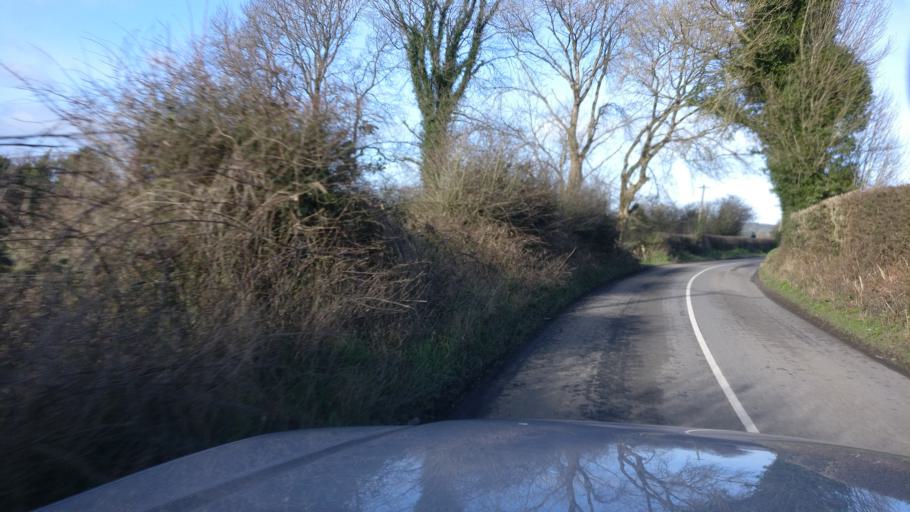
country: IE
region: Leinster
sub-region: Kilkenny
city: Castlecomer
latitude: 52.8818
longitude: -7.1632
